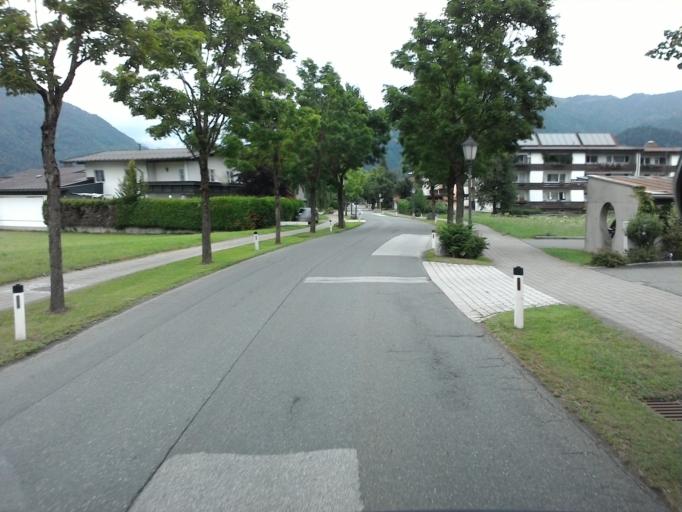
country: AT
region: Tyrol
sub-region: Politischer Bezirk Kitzbuhel
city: Kossen
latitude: 47.6625
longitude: 12.4045
